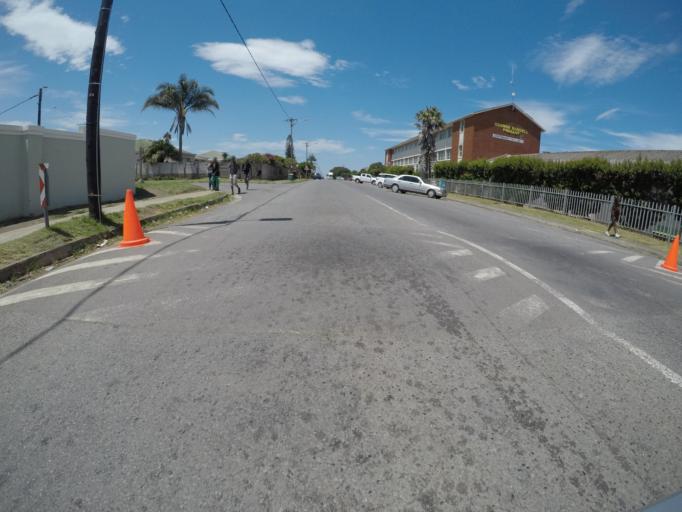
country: ZA
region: Eastern Cape
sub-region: Buffalo City Metropolitan Municipality
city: East London
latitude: -33.0354
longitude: 27.8560
